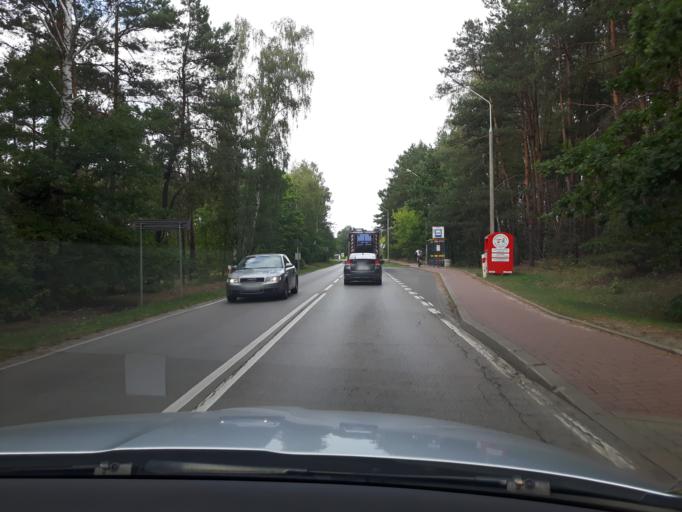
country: PL
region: Masovian Voivodeship
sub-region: Powiat legionowski
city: Stanislawow Pierwszy
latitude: 52.3854
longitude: 21.0301
